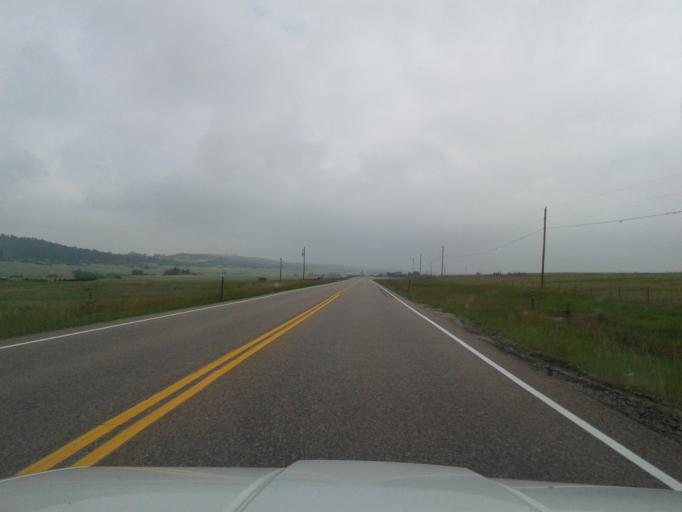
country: US
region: Colorado
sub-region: El Paso County
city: Woodmoor
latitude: 39.1864
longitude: -104.7310
